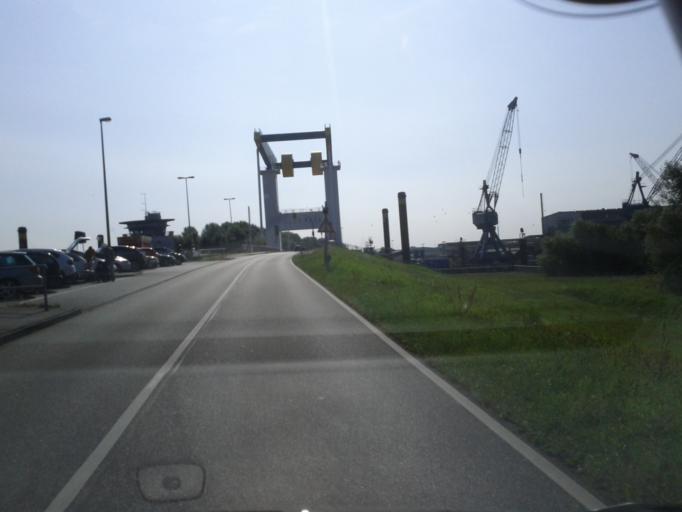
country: DE
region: Lower Saxony
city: Neu Wulmstorf
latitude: 53.5357
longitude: 9.7884
